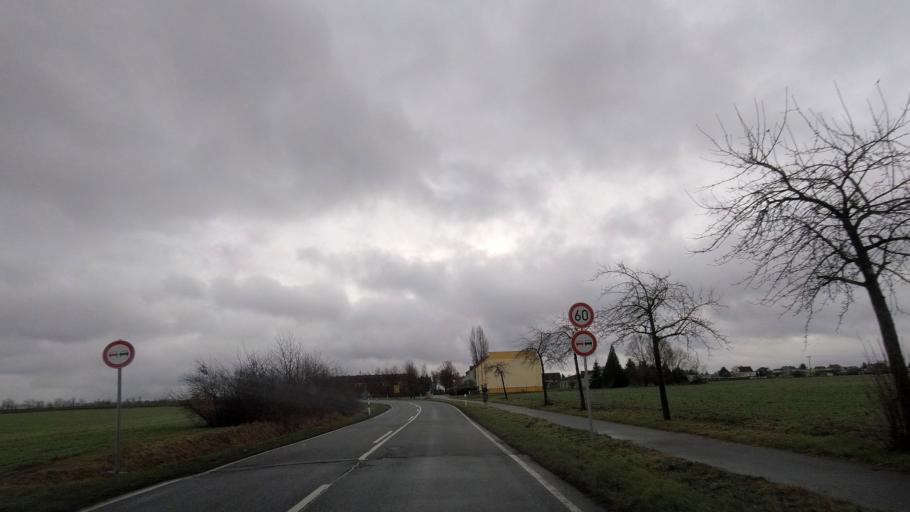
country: DE
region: Brandenburg
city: Niedergorsdorf
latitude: 51.9726
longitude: 12.9799
